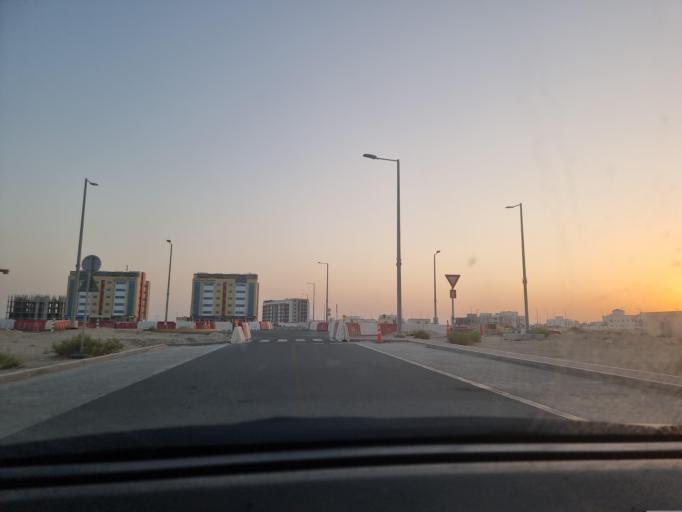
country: AE
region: Abu Dhabi
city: Abu Dhabi
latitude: 24.3706
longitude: 54.7410
